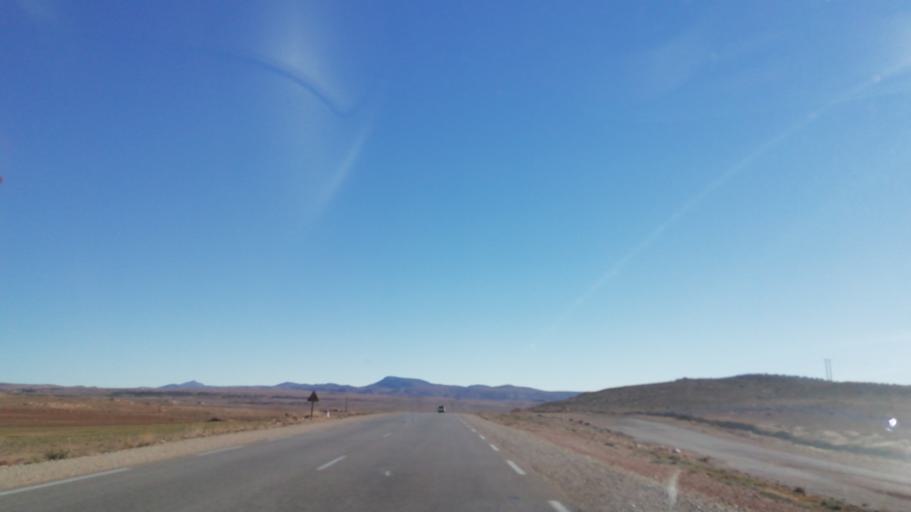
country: DZ
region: El Bayadh
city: El Bayadh
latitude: 33.6038
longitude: 1.2842
